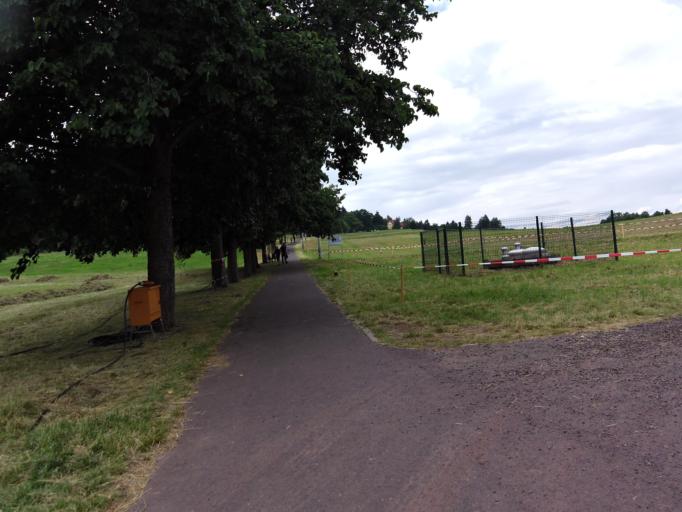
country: DE
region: Thuringia
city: Tabarz
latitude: 50.8748
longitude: 10.5116
